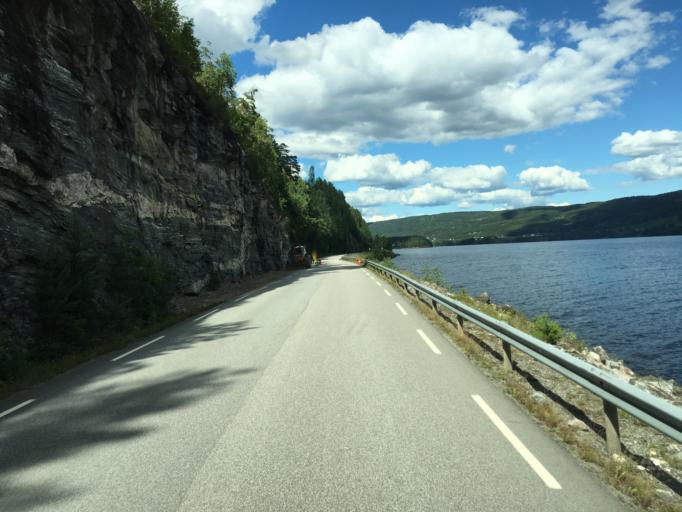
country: NO
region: Oppland
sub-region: Sondre Land
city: Hov
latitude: 60.6022
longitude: 10.3235
